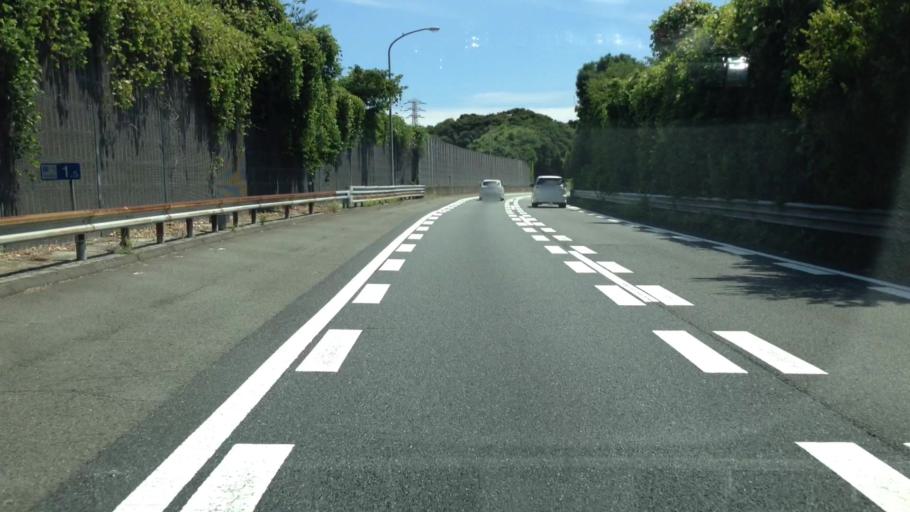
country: JP
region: Kanagawa
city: Yokohama
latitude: 35.4421
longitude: 139.5798
